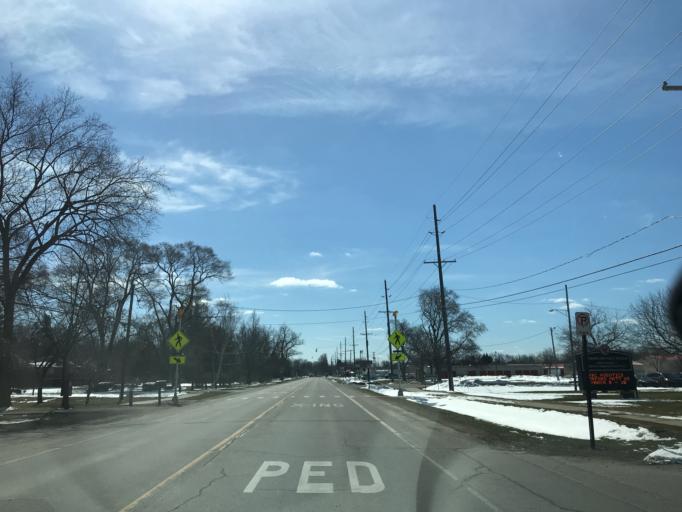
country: US
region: Michigan
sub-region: Livingston County
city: Whitmore Lake
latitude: 42.4141
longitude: -83.7611
